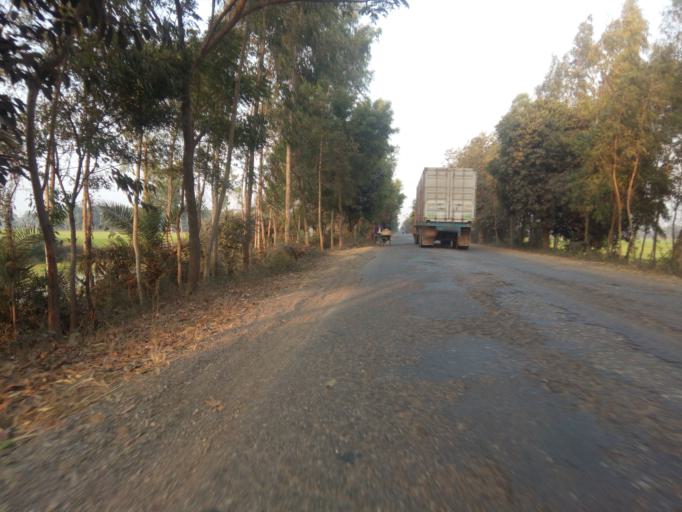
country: BD
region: Rajshahi
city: Bogra
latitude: 24.5591
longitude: 89.2008
